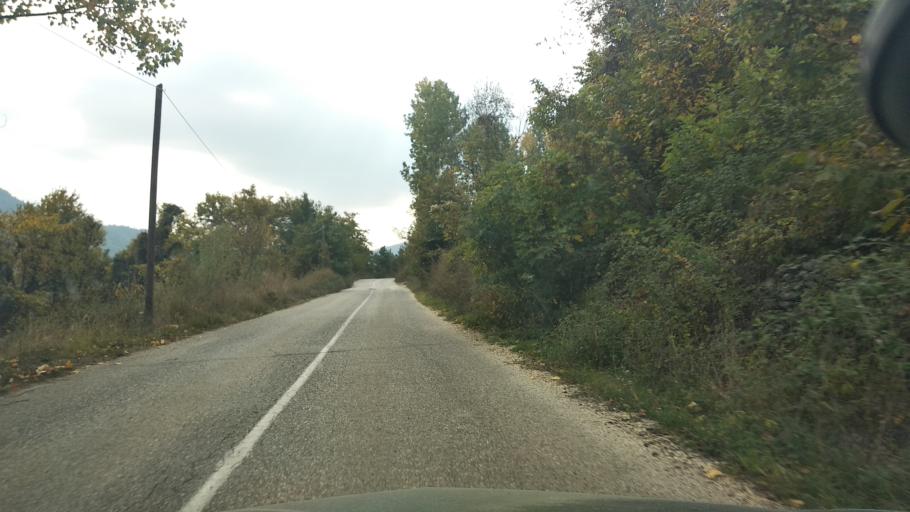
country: GR
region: Thessaly
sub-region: Trikala
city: Kastraki
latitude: 39.6733
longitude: 21.5093
